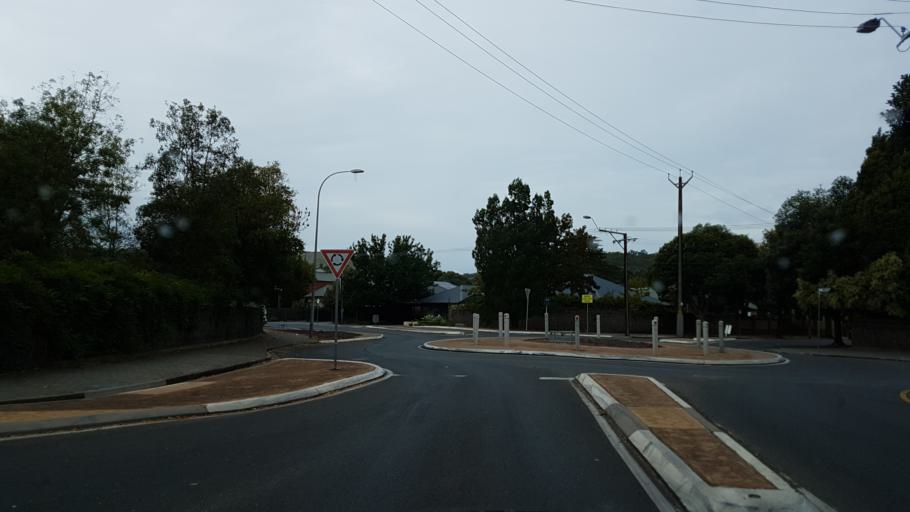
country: AU
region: South Australia
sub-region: Mitcham
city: Hawthorn
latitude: -34.9769
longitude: 138.6140
